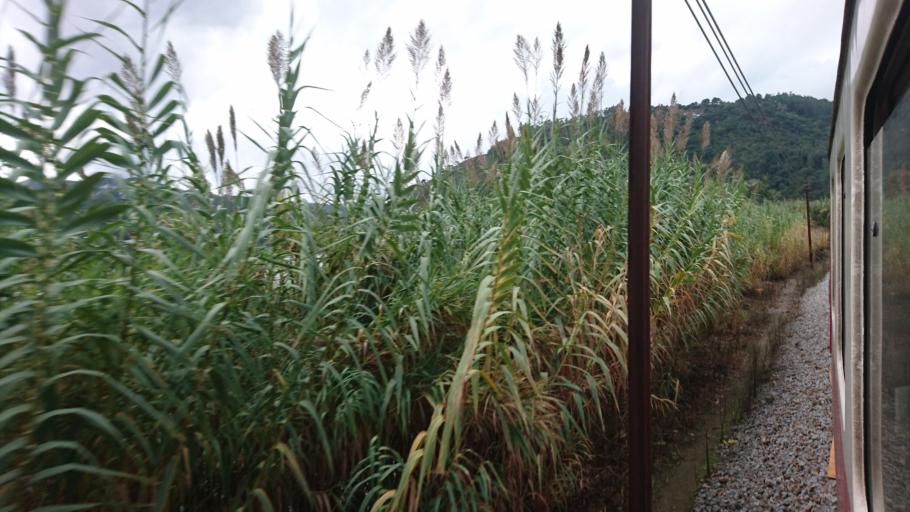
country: PT
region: Viseu
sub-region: Resende
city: Resende
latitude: 41.1062
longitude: -8.0115
